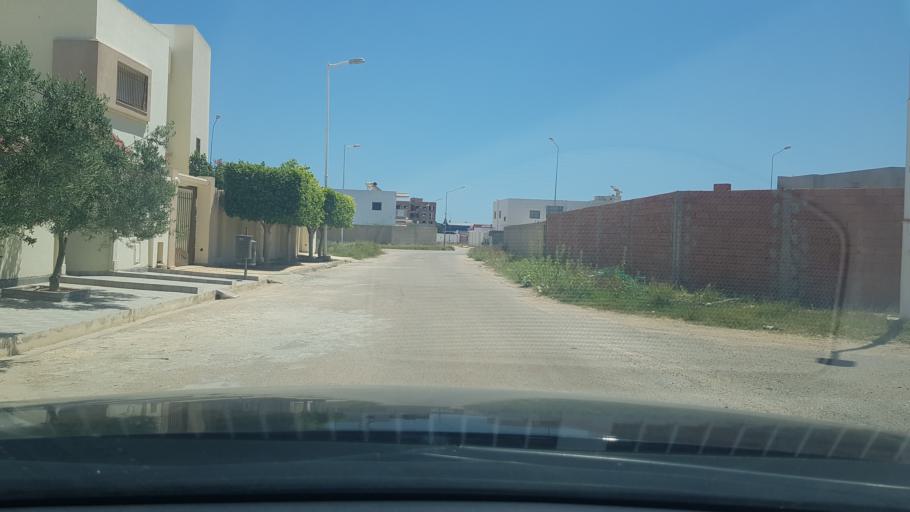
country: TN
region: Safaqis
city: Al Qarmadah
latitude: 34.8382
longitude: 10.7614
